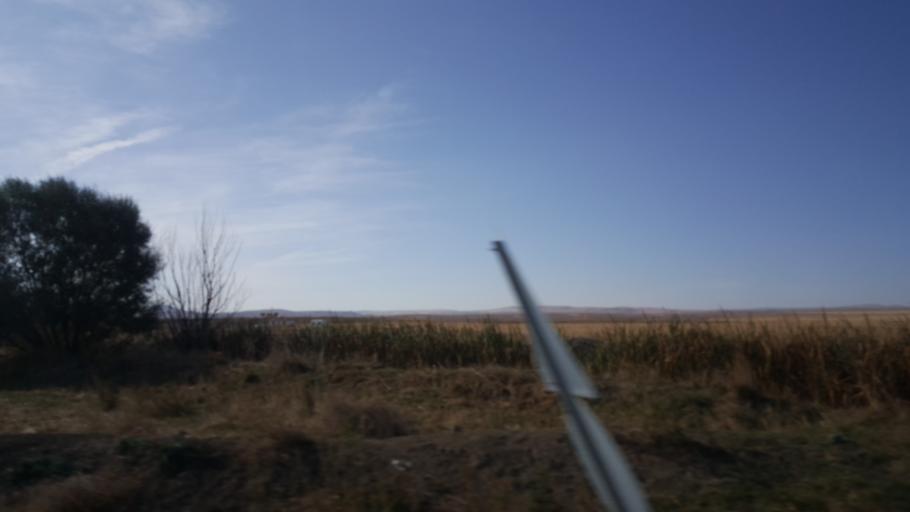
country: TR
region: Ankara
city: Yenice
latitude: 39.3674
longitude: 32.8106
